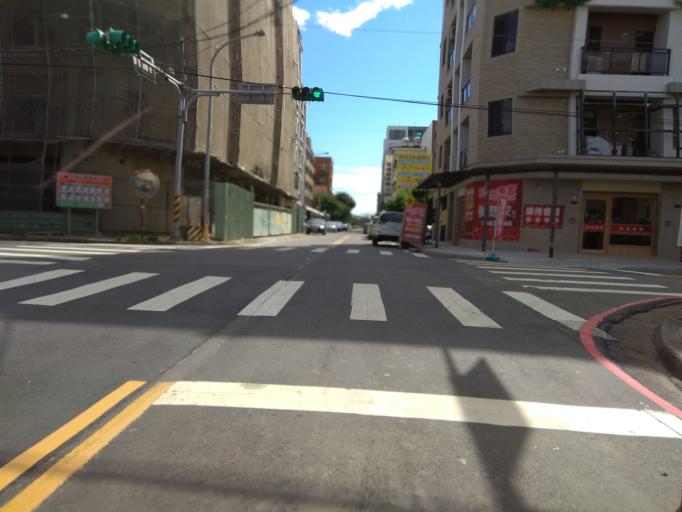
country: TW
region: Taiwan
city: Taoyuan City
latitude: 25.0500
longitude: 121.1197
